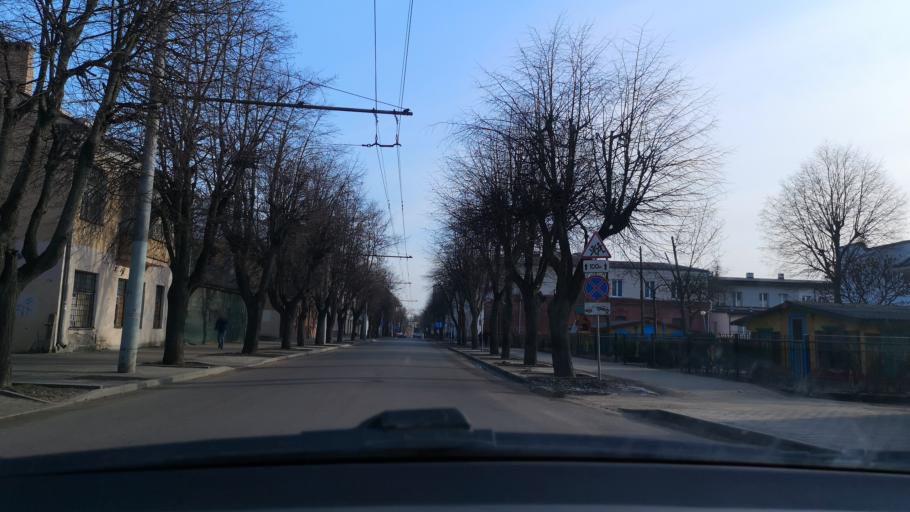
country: BY
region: Brest
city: Brest
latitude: 52.0964
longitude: 23.6869
